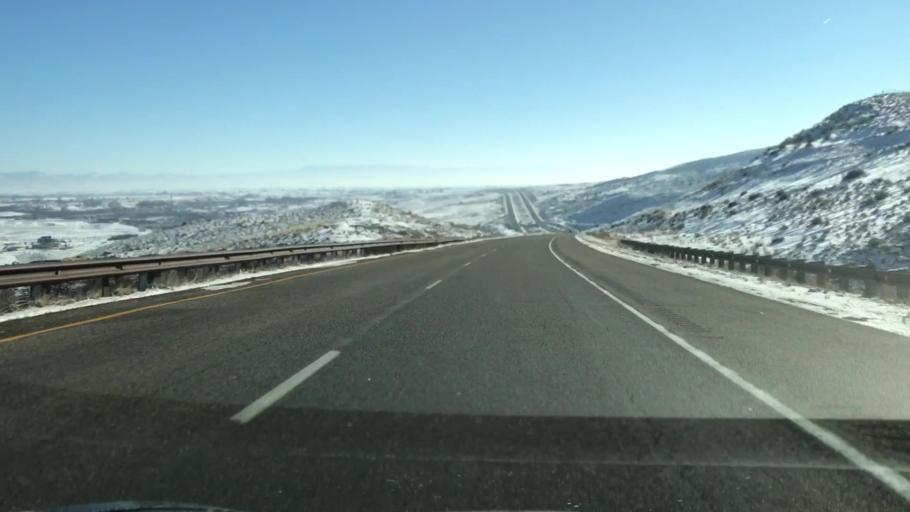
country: US
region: Colorado
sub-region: Mesa County
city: Loma
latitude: 39.2287
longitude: -108.9034
